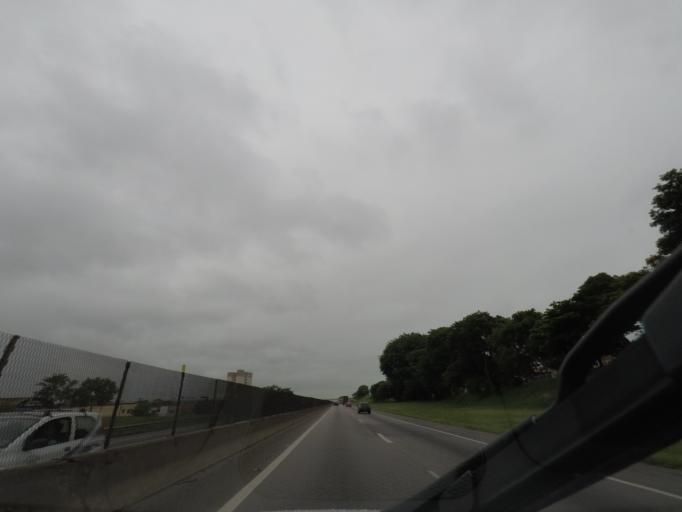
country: BR
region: Sao Paulo
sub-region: Taubate
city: Taubate
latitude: -23.0273
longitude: -45.5433
